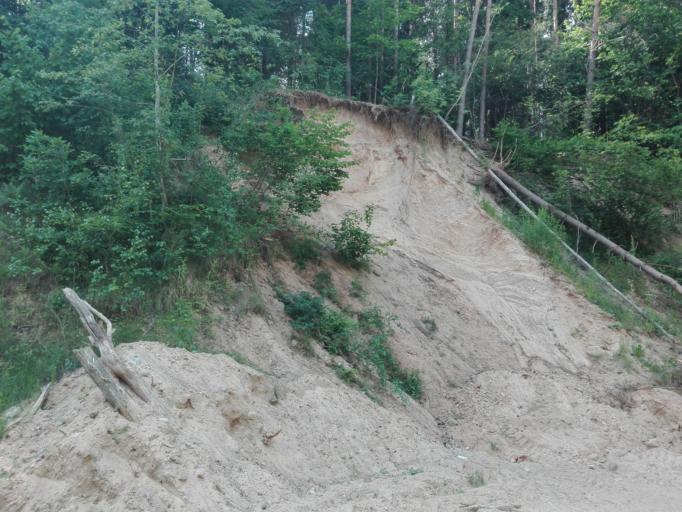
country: LT
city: Skaidiskes
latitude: 54.5260
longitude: 25.6223
